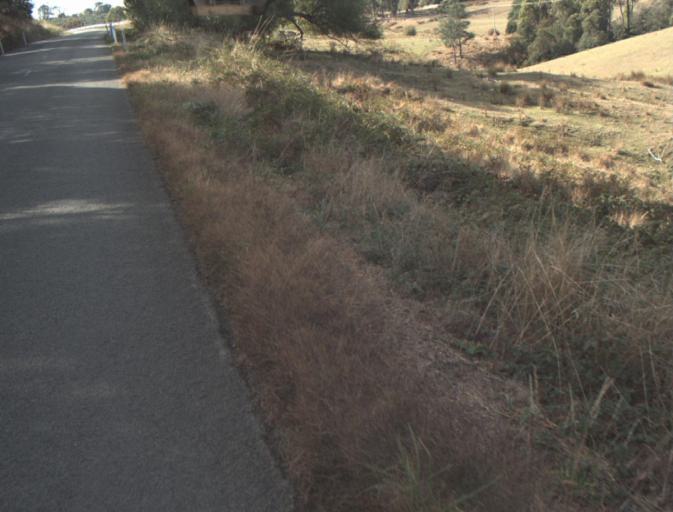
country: AU
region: Tasmania
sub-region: Launceston
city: Mayfield
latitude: -41.1849
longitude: 147.2220
